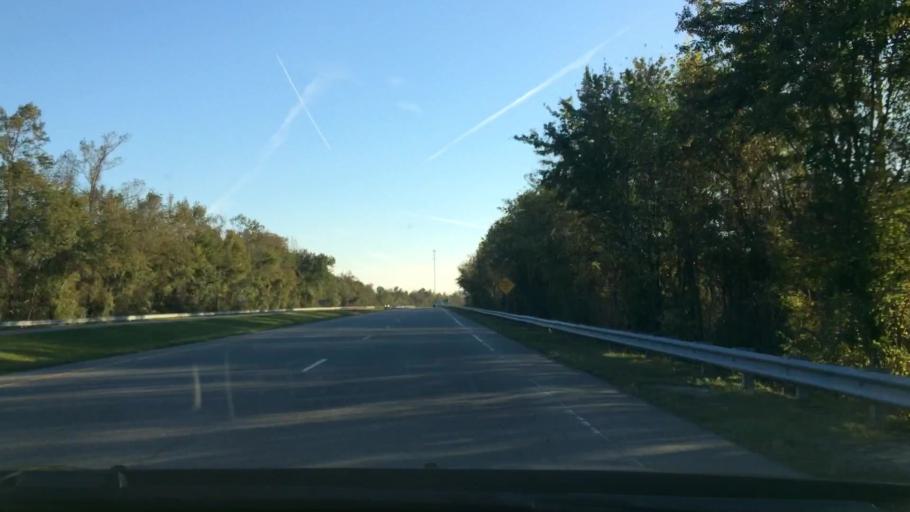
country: US
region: North Carolina
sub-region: Pitt County
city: Grifton
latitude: 35.3836
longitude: -77.4491
